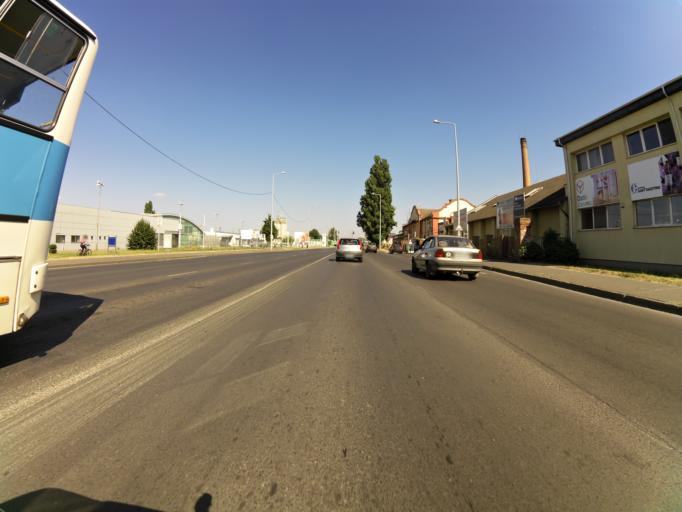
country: HU
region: Csongrad
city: Szeged
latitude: 46.2662
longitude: 20.1115
